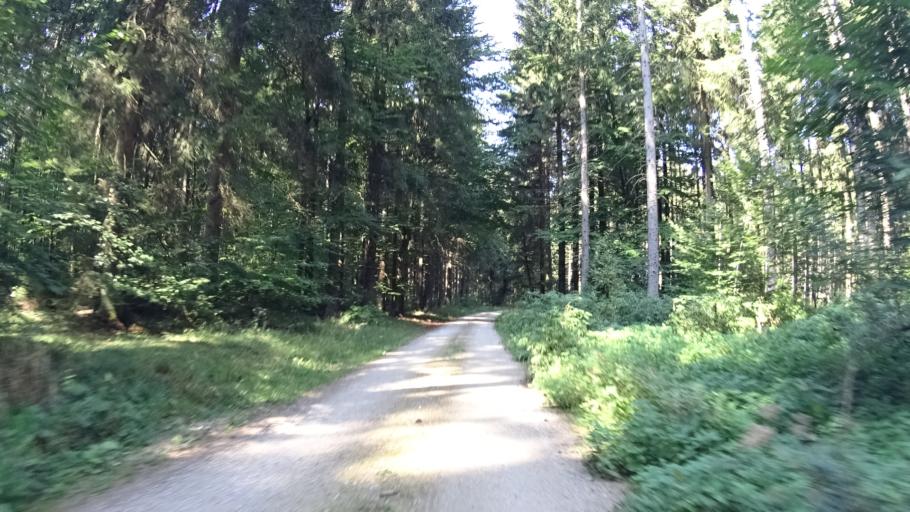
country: DE
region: Bavaria
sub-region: Upper Bavaria
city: Walting
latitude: 48.9648
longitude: 11.3571
